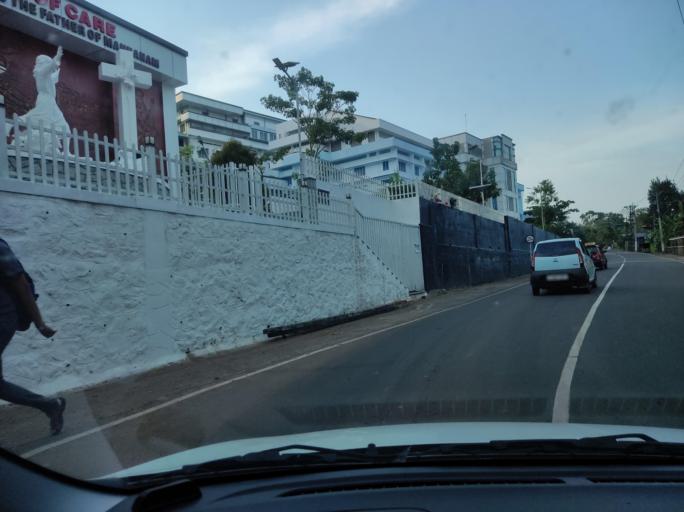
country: IN
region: Kerala
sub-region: Kottayam
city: Kottayam
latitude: 9.6467
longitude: 76.5241
